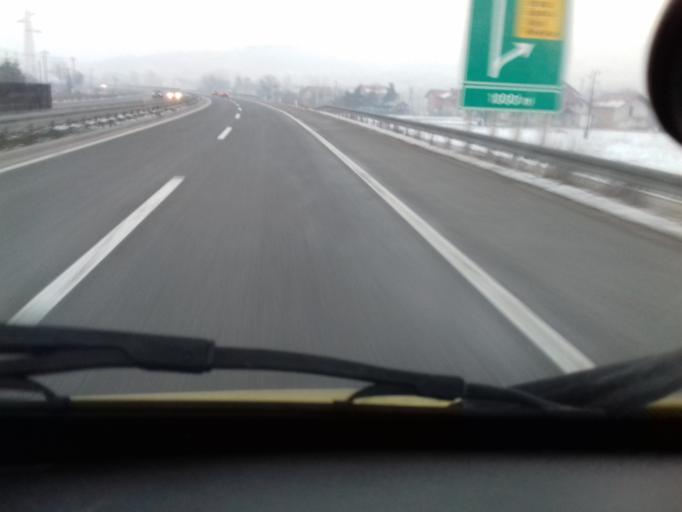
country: BA
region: Federation of Bosnia and Herzegovina
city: Ilijas
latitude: 43.9588
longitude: 18.2583
